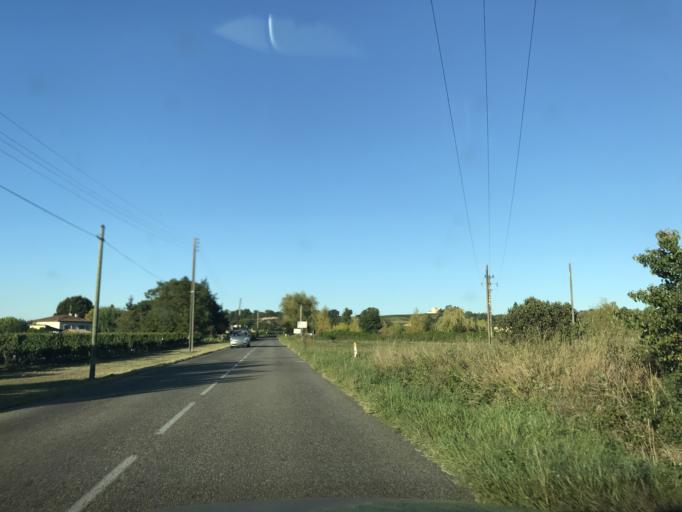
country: FR
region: Aquitaine
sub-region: Departement de la Gironde
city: Mouliets-et-Villemartin
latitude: 44.8089
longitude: -0.0413
